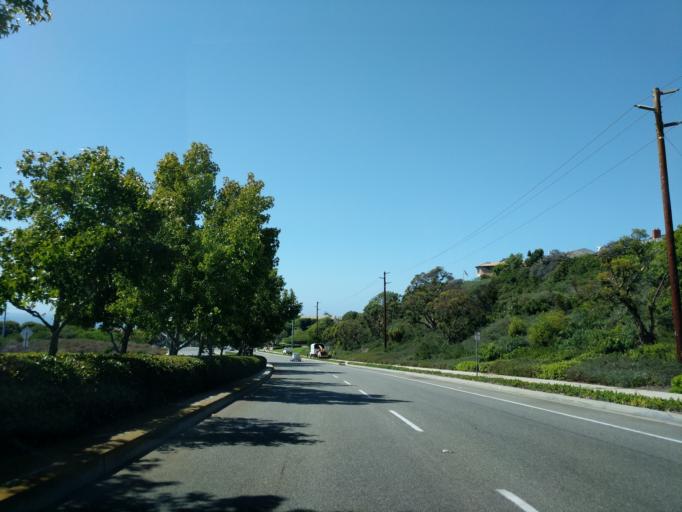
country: US
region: California
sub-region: Orange County
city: San Joaquin Hills
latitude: 33.6075
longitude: -117.8485
